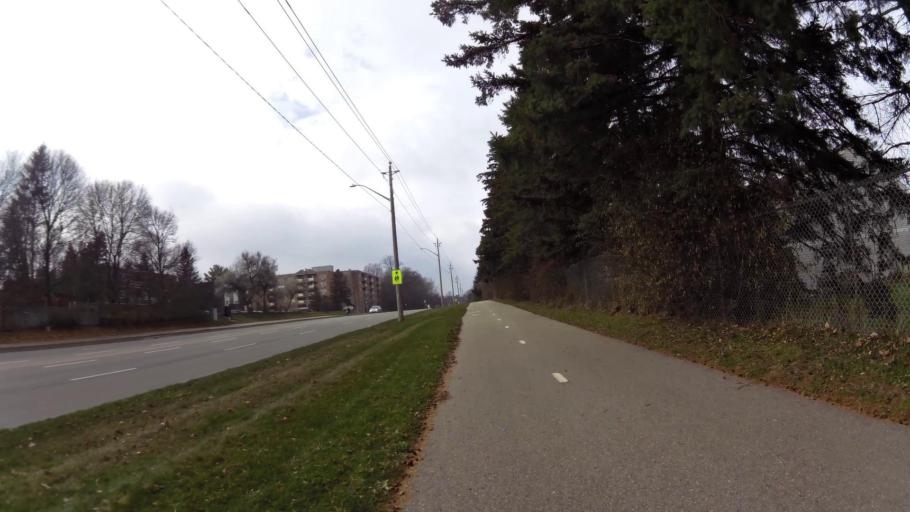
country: CA
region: Ontario
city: Kitchener
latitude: 43.4177
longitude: -80.4742
